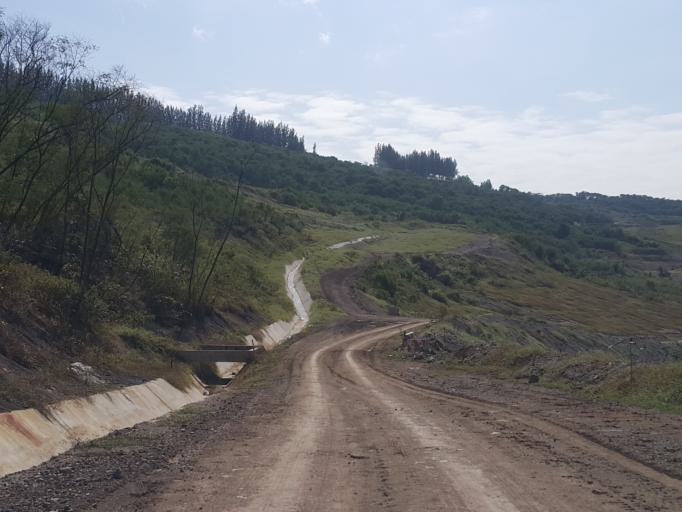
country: TH
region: Lampang
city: Mae Mo
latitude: 18.3243
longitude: 99.7375
